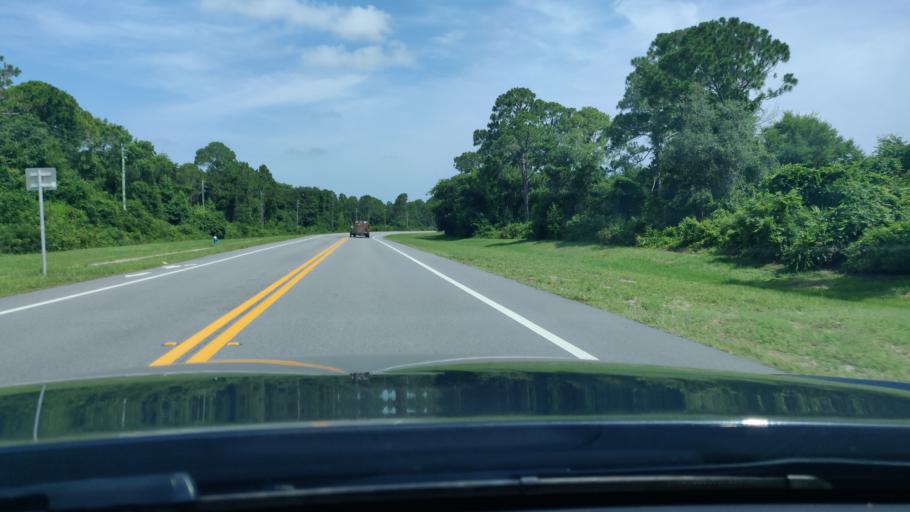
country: US
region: Florida
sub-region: Flagler County
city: Palm Coast
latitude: 29.5351
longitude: -81.1720
